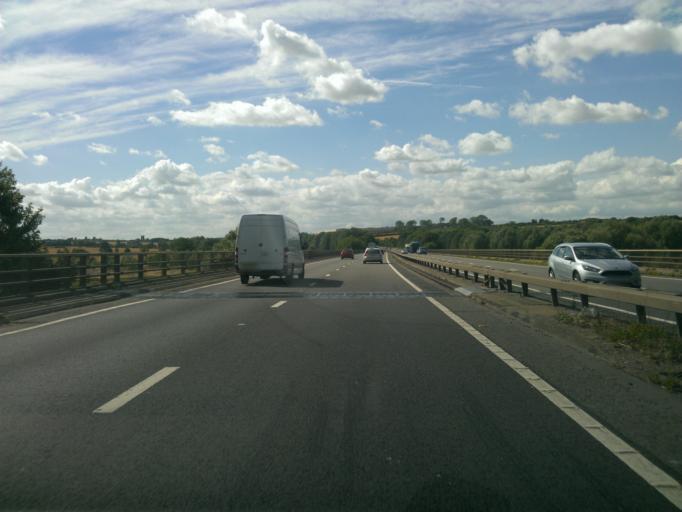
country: GB
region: England
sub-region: Northamptonshire
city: Thrapston
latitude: 52.3893
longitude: -0.5388
